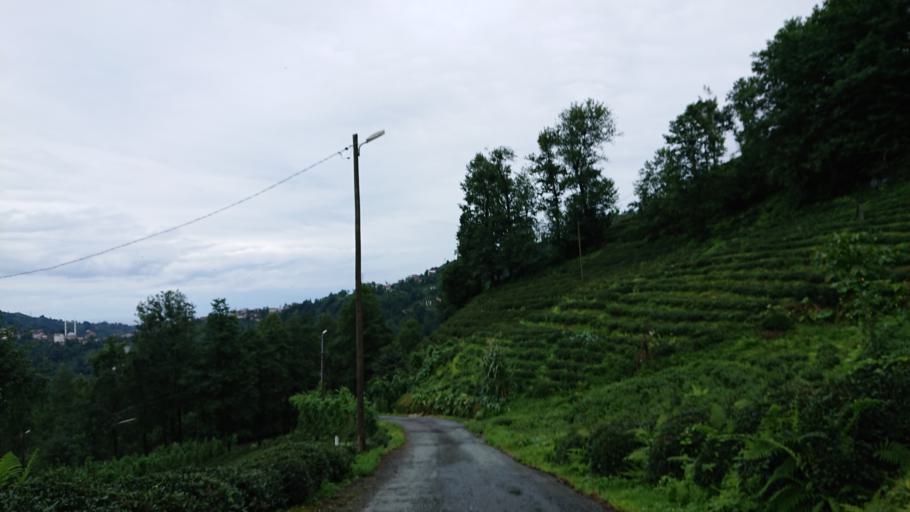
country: TR
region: Rize
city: Rize
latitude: 40.9854
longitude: 40.4844
